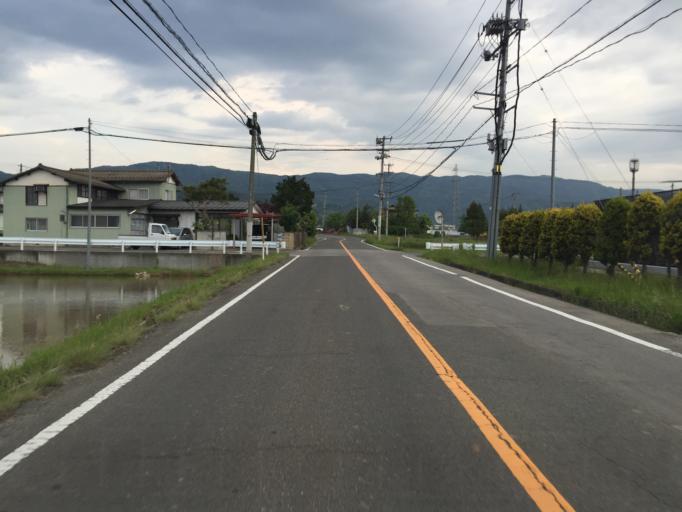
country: JP
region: Fukushima
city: Hobaramachi
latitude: 37.8693
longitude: 140.5469
